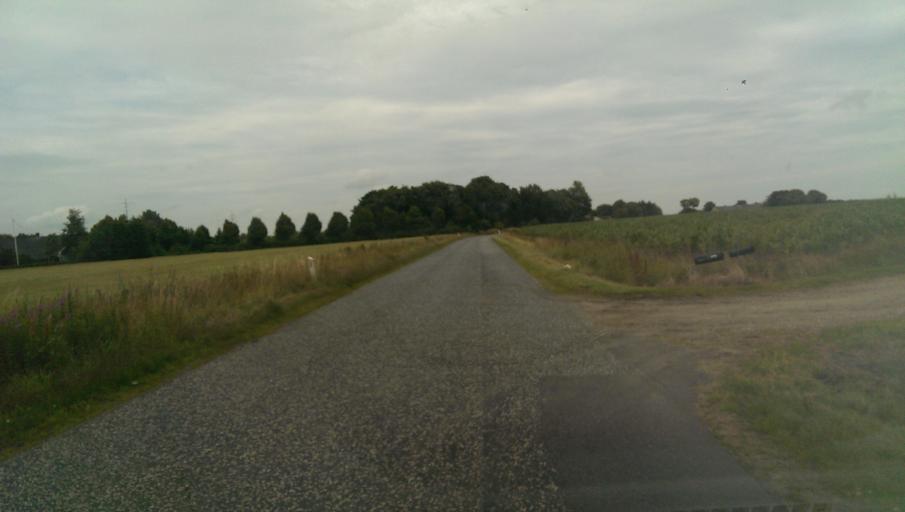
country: DK
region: South Denmark
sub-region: Esbjerg Kommune
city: Bramming
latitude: 55.4670
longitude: 8.7230
